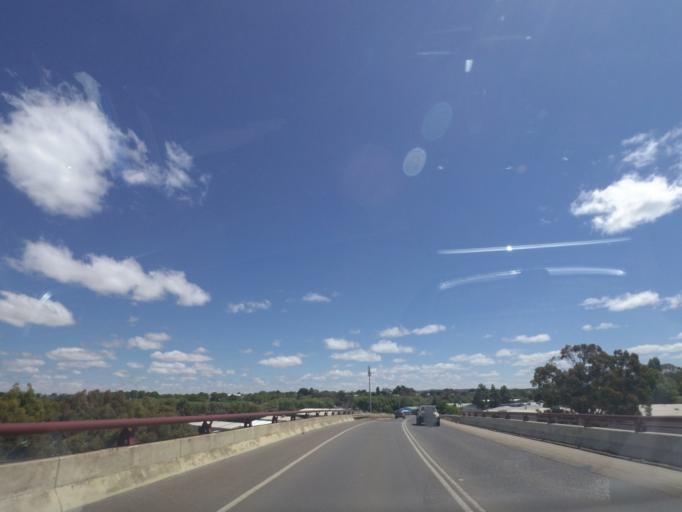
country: AU
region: Victoria
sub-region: Mount Alexander
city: Castlemaine
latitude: -37.2390
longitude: 144.4569
